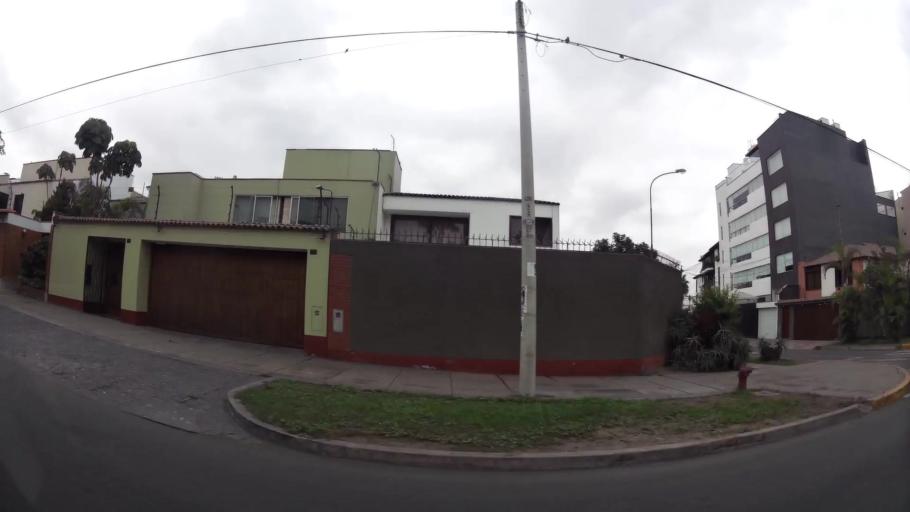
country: PE
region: Lima
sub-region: Lima
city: Surco
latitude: -12.1210
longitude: -76.9848
